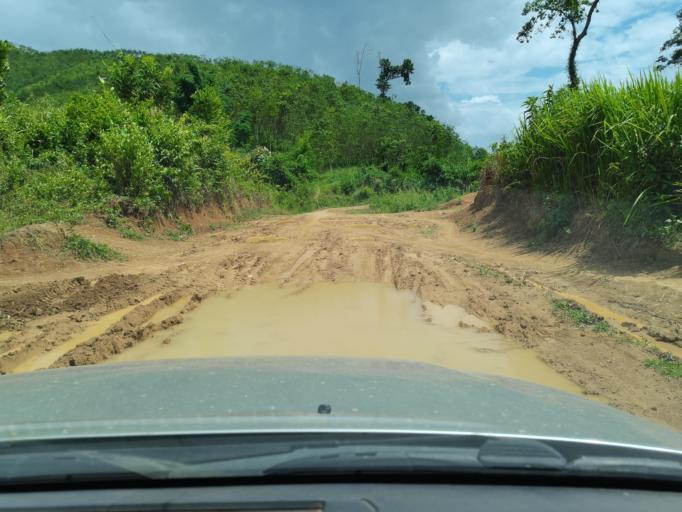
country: LA
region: Loungnamtha
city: Muang Long
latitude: 20.7215
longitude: 101.0142
